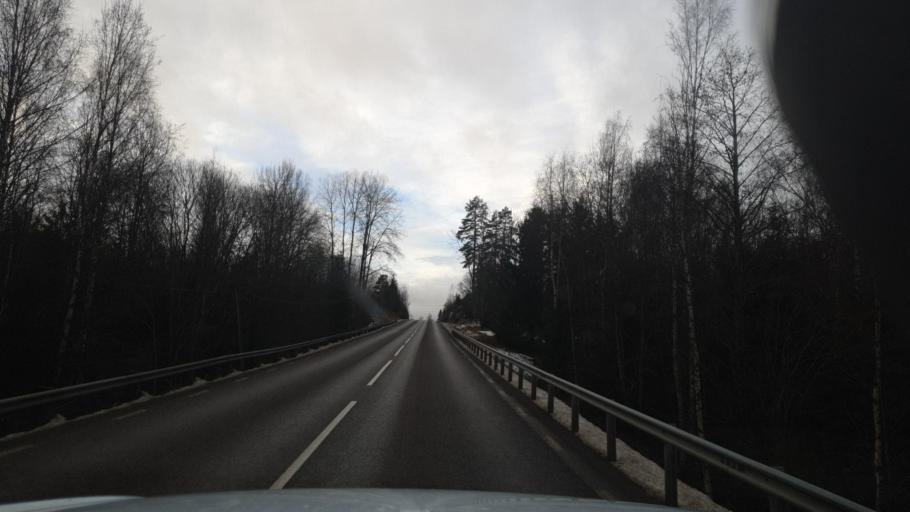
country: SE
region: Vaermland
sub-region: Eda Kommun
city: Amotfors
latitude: 59.6893
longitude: 12.4230
